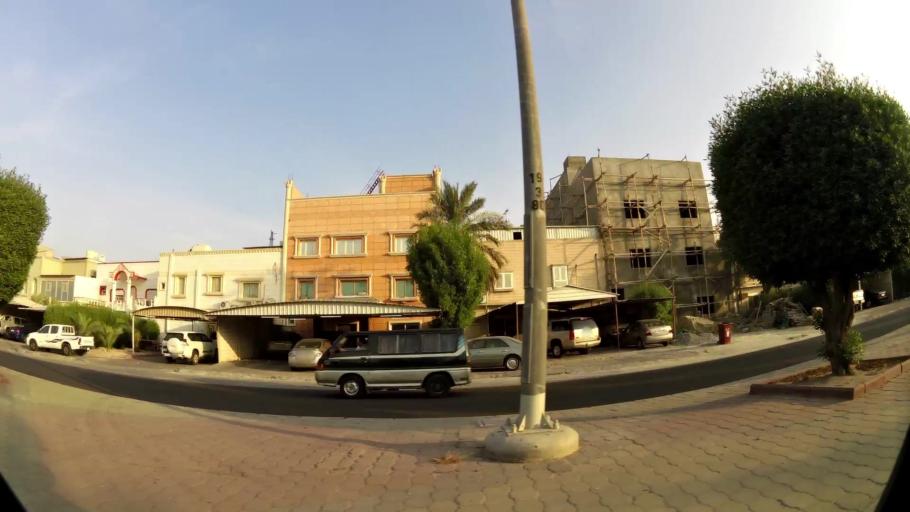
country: KW
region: Mubarak al Kabir
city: Sabah as Salim
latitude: 29.2467
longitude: 48.0641
